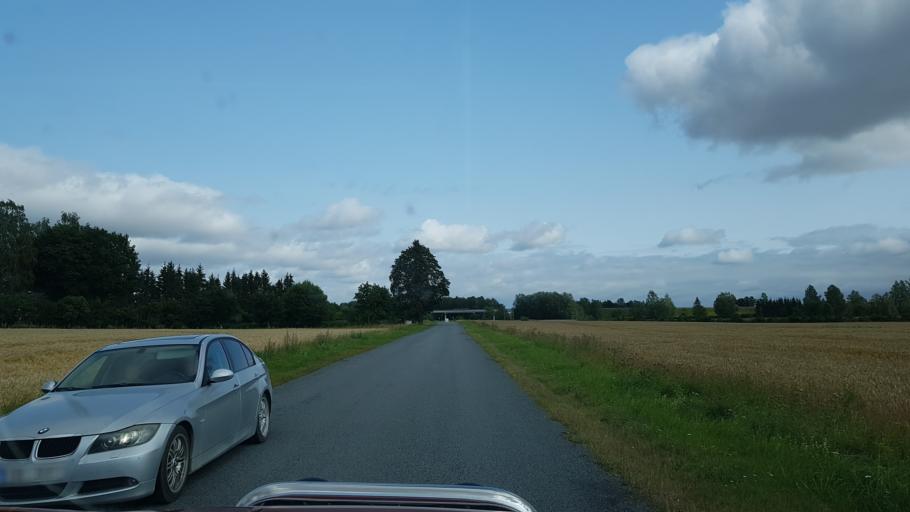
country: EE
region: Laeaene-Virumaa
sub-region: Kadrina vald
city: Kadrina
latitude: 59.3382
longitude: 26.1087
